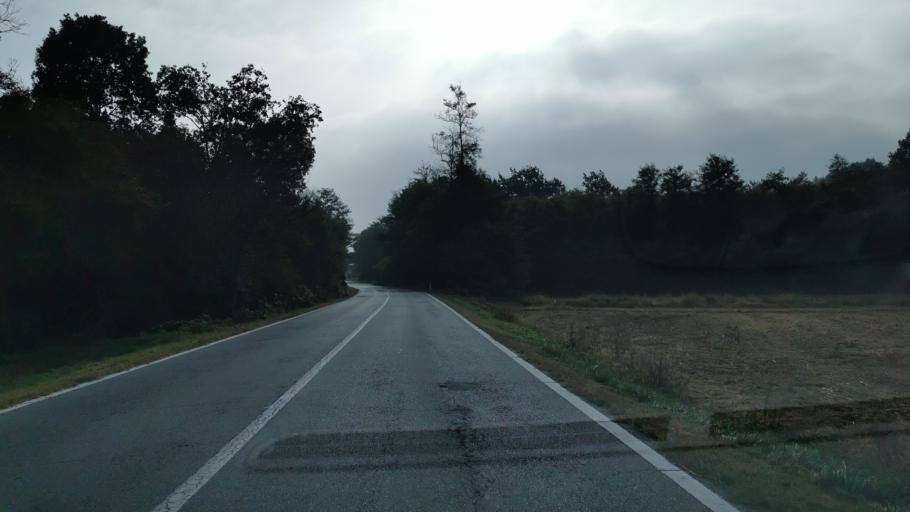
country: IT
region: Piedmont
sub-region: Provincia di Torino
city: Front
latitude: 45.2682
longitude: 7.6842
